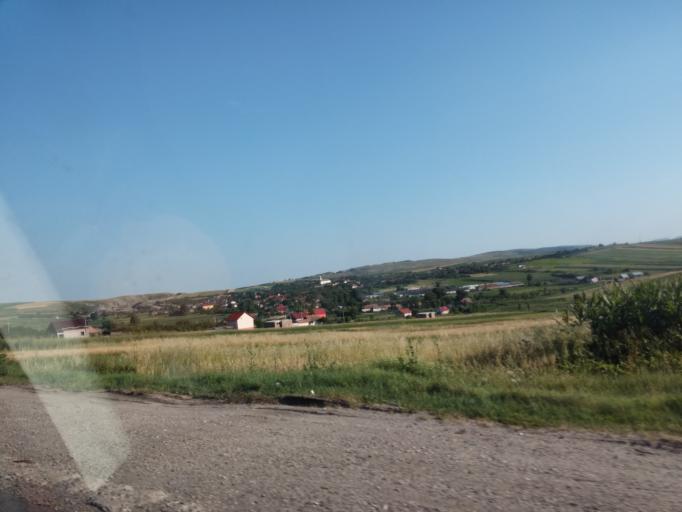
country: RO
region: Cluj
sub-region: Comuna Tureni
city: Tureni
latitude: 46.6331
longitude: 23.6952
